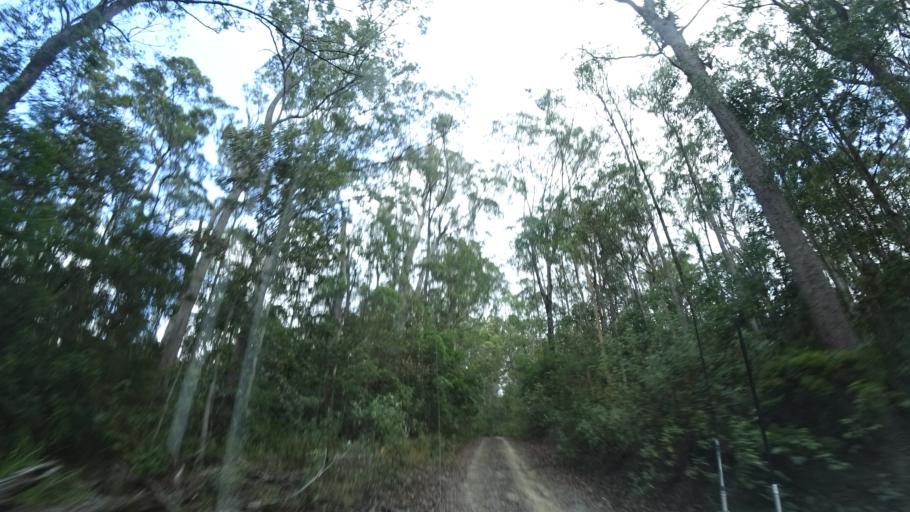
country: AU
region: Queensland
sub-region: Moreton Bay
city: Highvale
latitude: -27.4203
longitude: 152.8182
